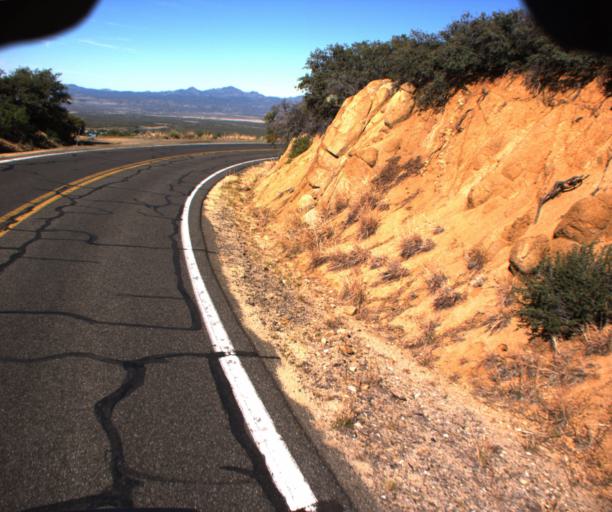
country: US
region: Arizona
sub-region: Yavapai County
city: Prescott
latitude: 34.4233
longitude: -112.5739
